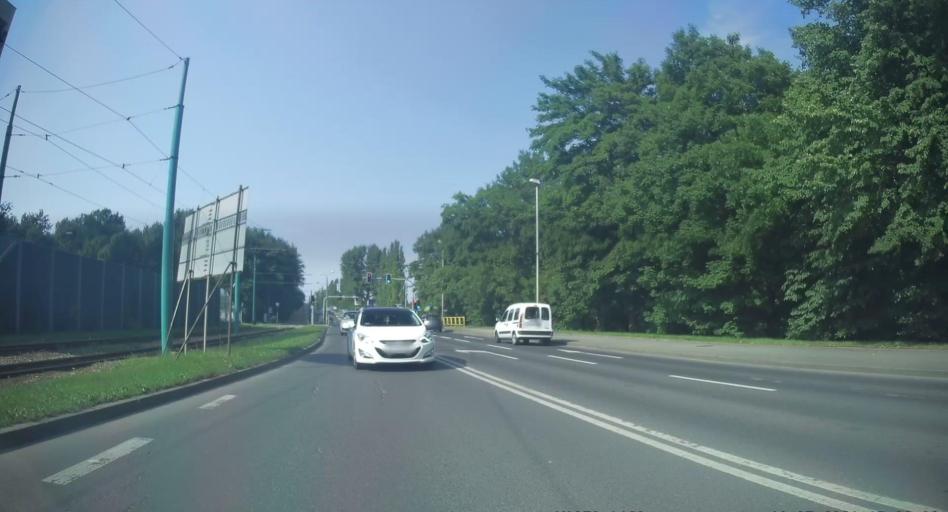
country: PL
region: Silesian Voivodeship
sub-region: Swietochlowice
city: Swietochlowice
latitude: 50.2977
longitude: 18.9176
